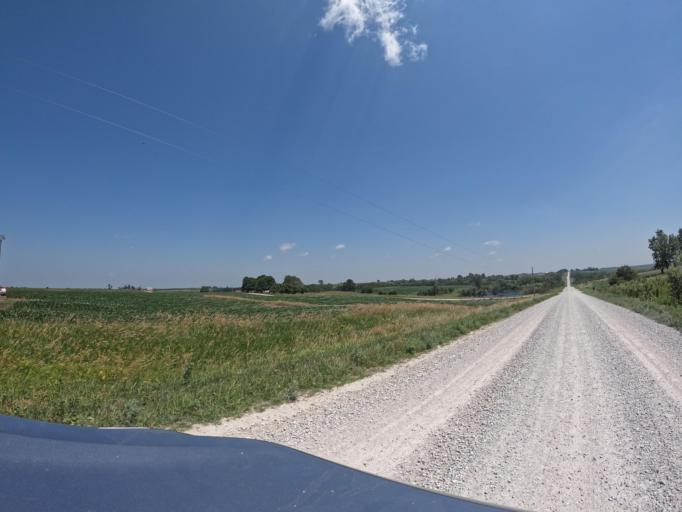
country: US
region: Iowa
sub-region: Keokuk County
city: Sigourney
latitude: 41.2579
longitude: -92.1820
